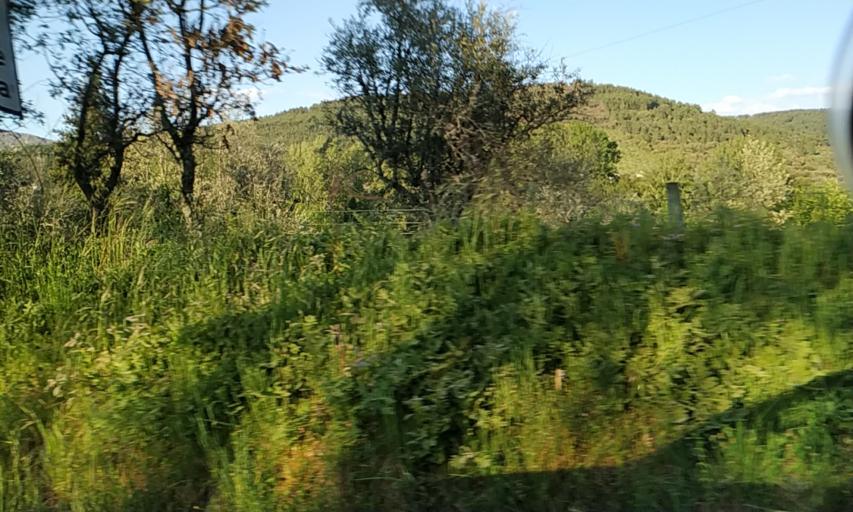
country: PT
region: Portalegre
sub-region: Marvao
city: Marvao
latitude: 39.3719
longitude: -7.3883
